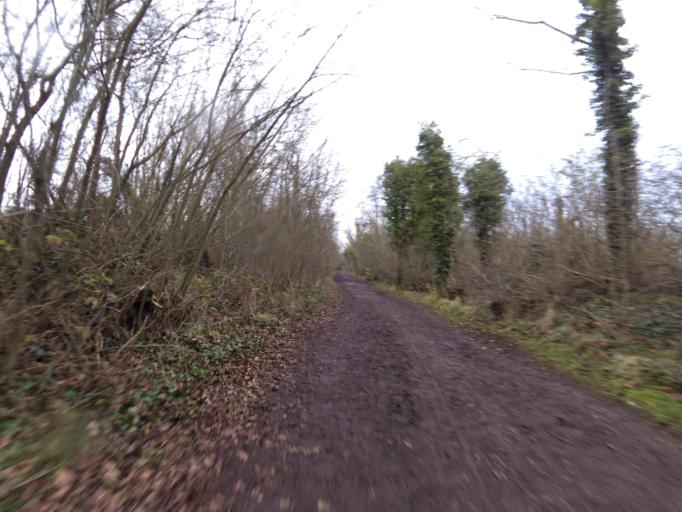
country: GB
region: England
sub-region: Cambridgeshire
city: Waterbeach
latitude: 52.2386
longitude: 0.1678
